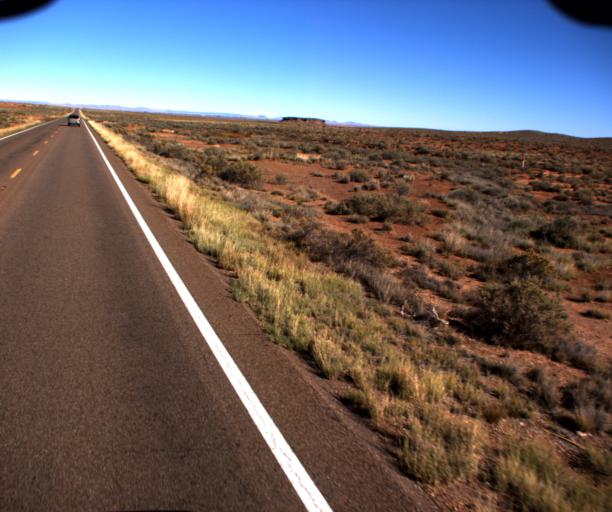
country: US
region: Arizona
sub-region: Navajo County
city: Holbrook
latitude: 34.8146
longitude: -110.1391
